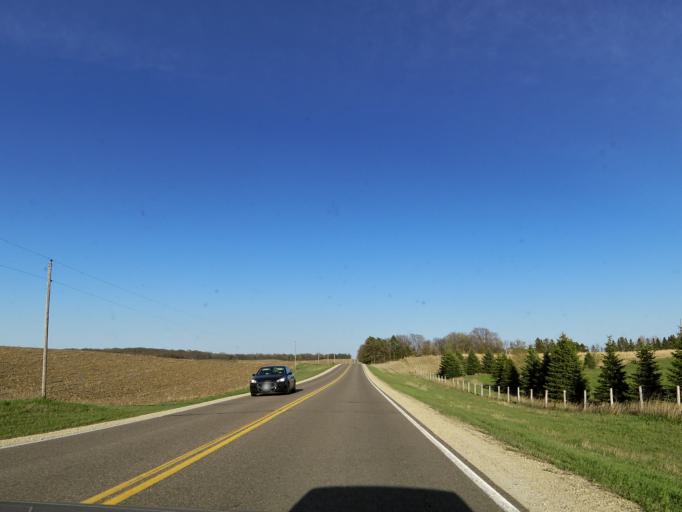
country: US
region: Minnesota
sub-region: Rice County
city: Northfield
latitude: 44.5436
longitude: -93.1292
